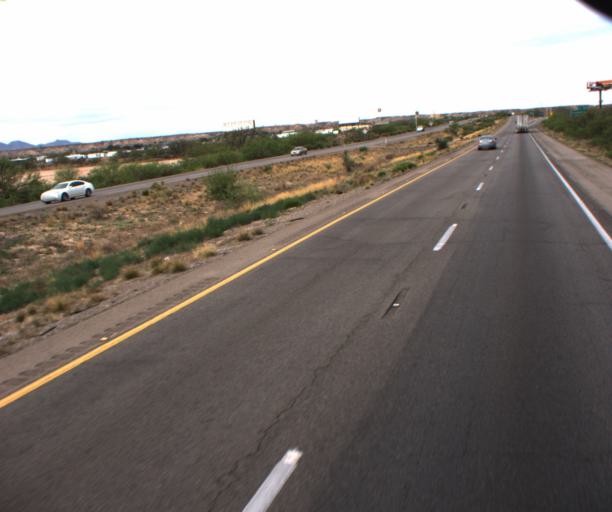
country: US
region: Arizona
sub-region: Cochise County
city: Benson
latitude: 31.9787
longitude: -110.2998
